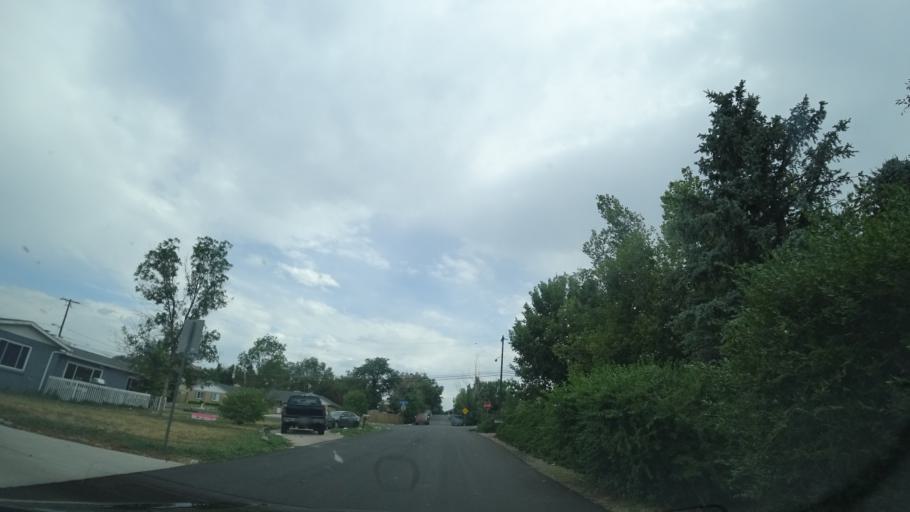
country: US
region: Colorado
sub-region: Jefferson County
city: Lakewood
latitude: 39.7153
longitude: -105.0827
